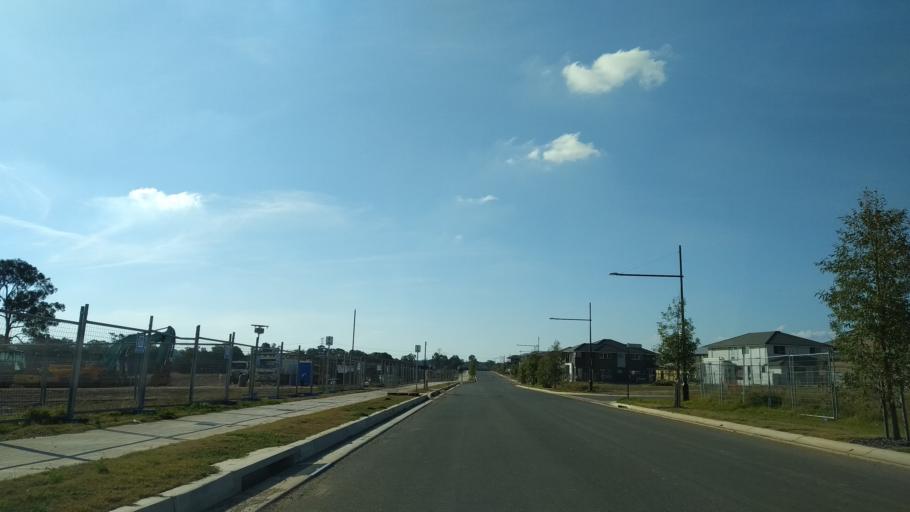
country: AU
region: New South Wales
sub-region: Blacktown
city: Blackett
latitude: -33.6929
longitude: 150.8059
